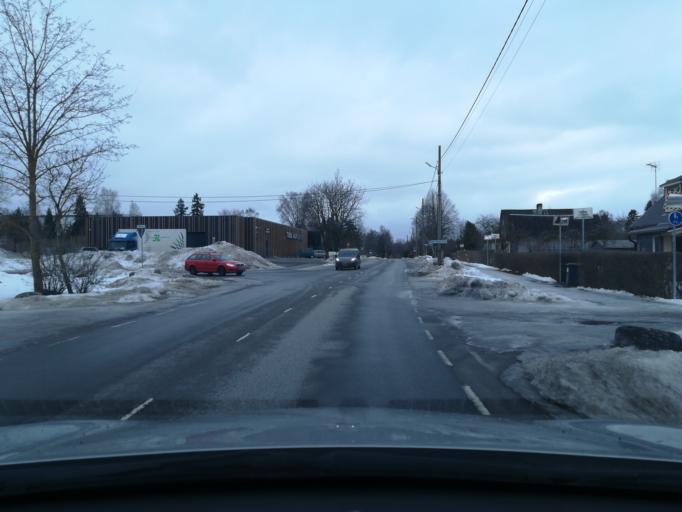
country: EE
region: Harju
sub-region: Nissi vald
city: Turba
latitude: 59.0813
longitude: 24.2360
